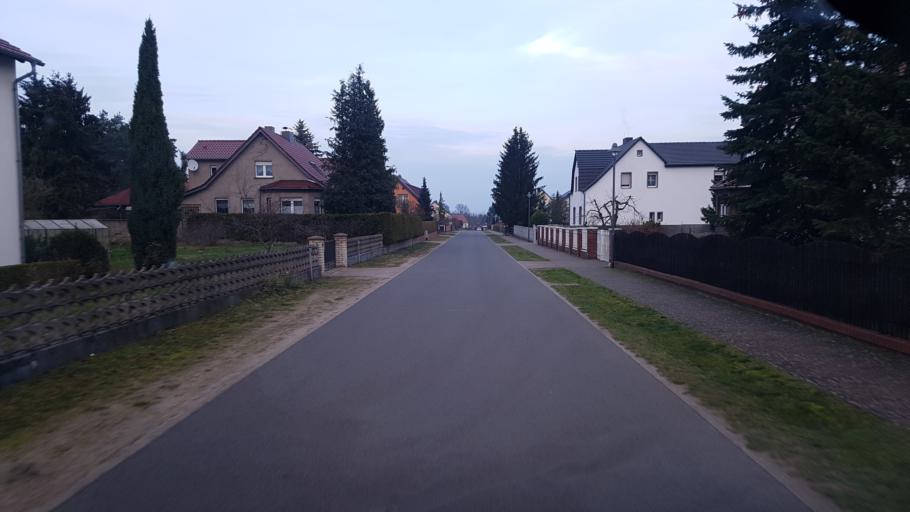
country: DE
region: Brandenburg
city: Ziltendorf
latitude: 52.2018
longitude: 14.6177
